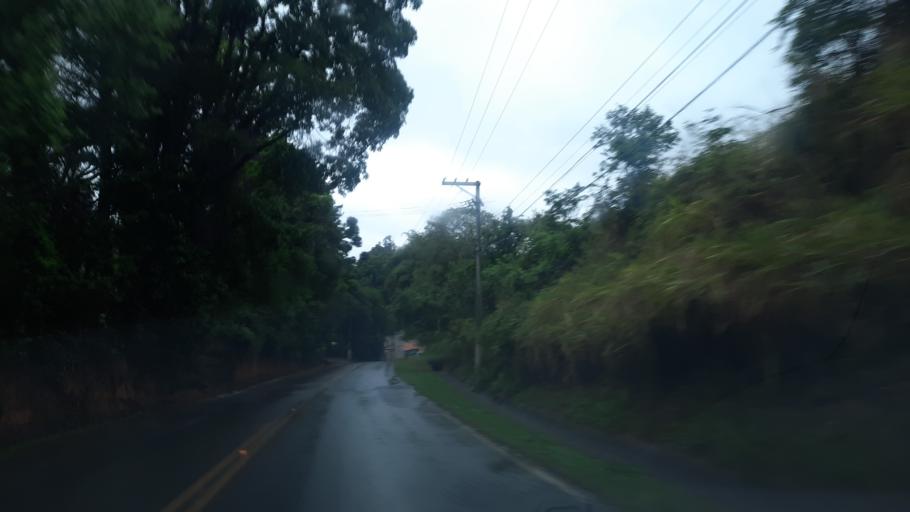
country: BR
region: Sao Paulo
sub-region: Atibaia
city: Atibaia
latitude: -23.0858
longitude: -46.5302
